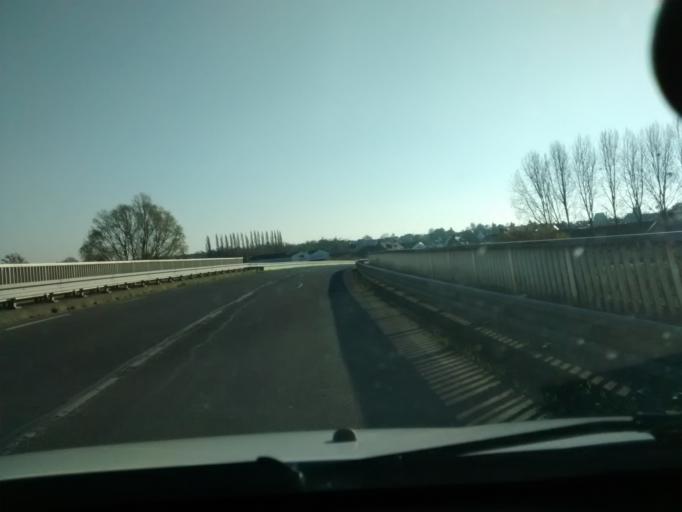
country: FR
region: Lower Normandy
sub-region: Departement de la Manche
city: Pontorson
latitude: 48.5628
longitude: -1.5101
